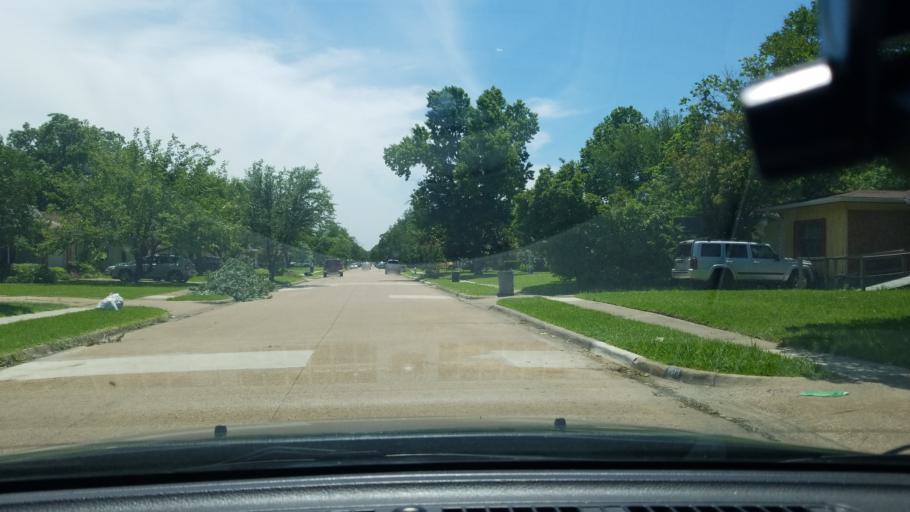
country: US
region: Texas
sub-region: Dallas County
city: Mesquite
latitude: 32.7868
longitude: -96.6128
